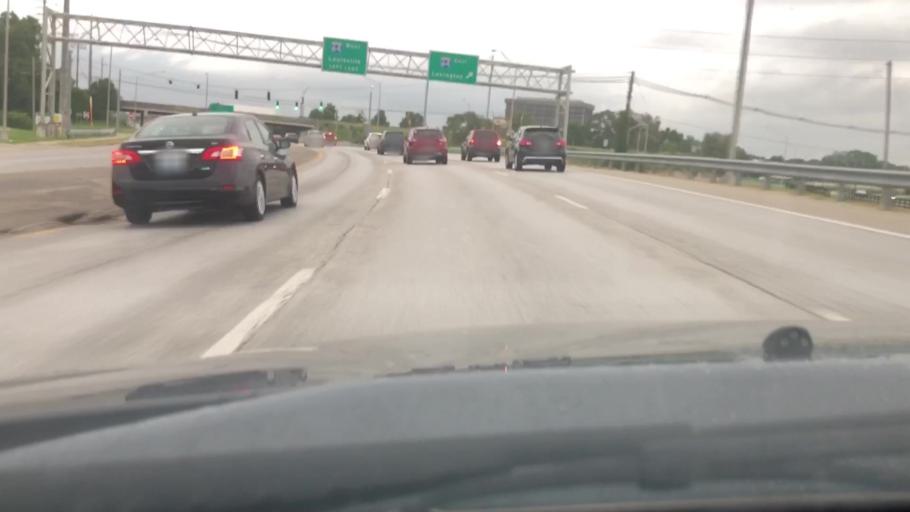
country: US
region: Kentucky
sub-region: Jefferson County
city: Hurstbourne Acres
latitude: 38.2214
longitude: -85.5800
